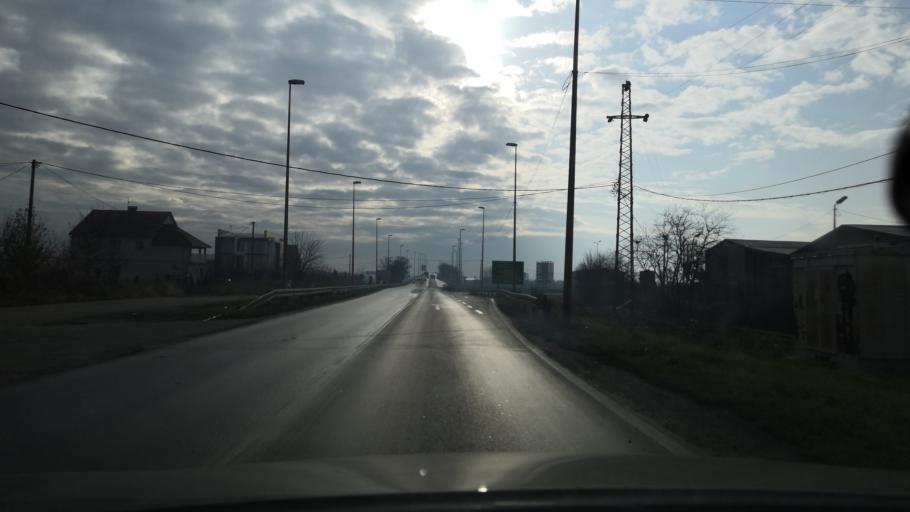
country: RS
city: Dobanovci
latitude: 44.8481
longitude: 20.2089
